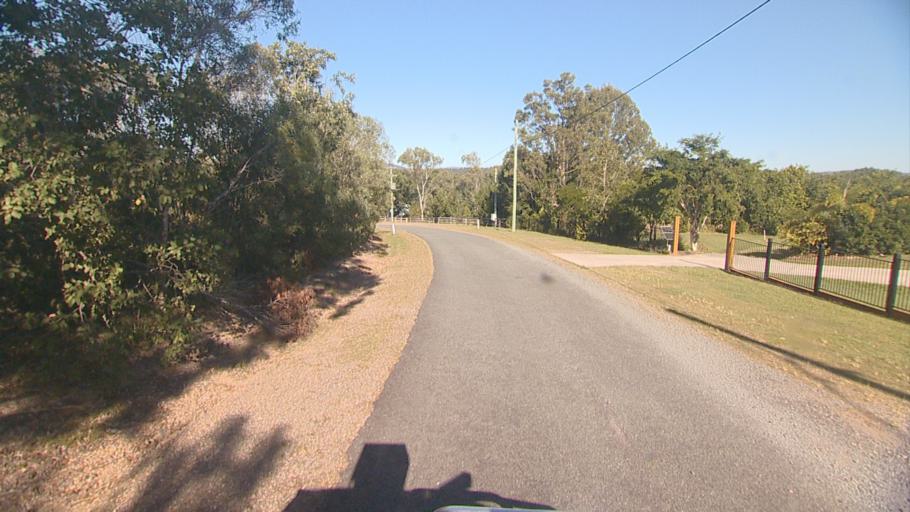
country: AU
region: Queensland
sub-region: Logan
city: Logan Reserve
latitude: -27.7443
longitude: 153.1236
